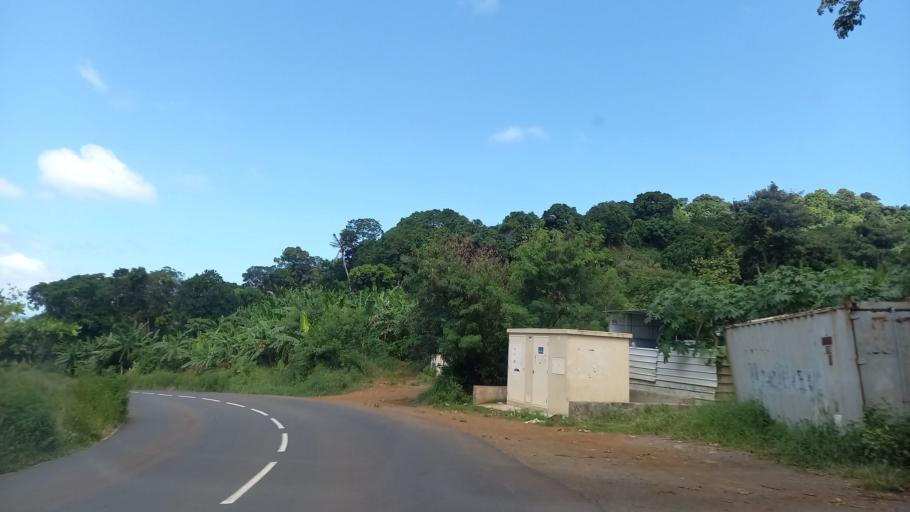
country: YT
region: Acoua
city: Acoua
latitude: -12.7385
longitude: 45.0532
